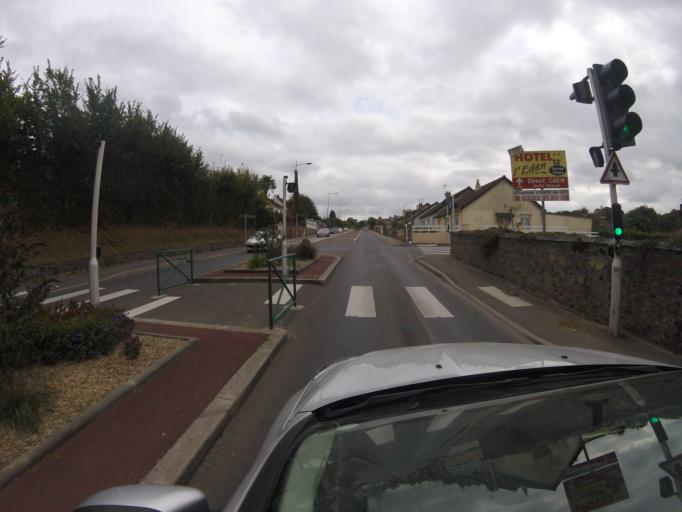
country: FR
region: Lower Normandy
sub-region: Departement de la Manche
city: Cherbourg-Octeville
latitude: 49.6159
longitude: -1.6063
